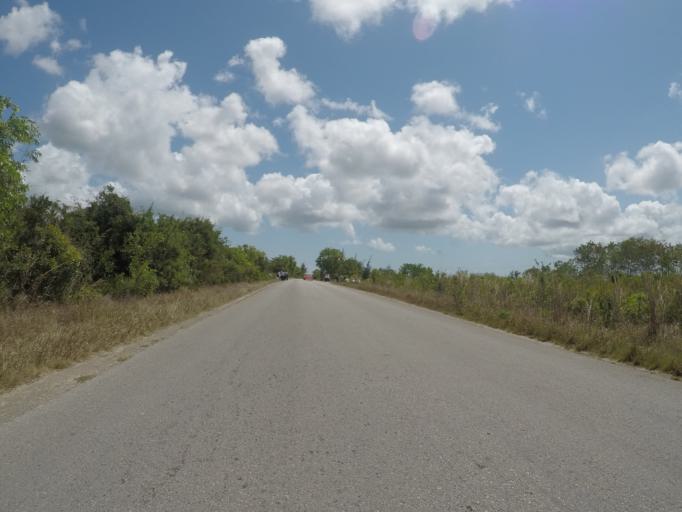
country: TZ
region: Zanzibar Central/South
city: Nganane
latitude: -6.2815
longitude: 39.4733
